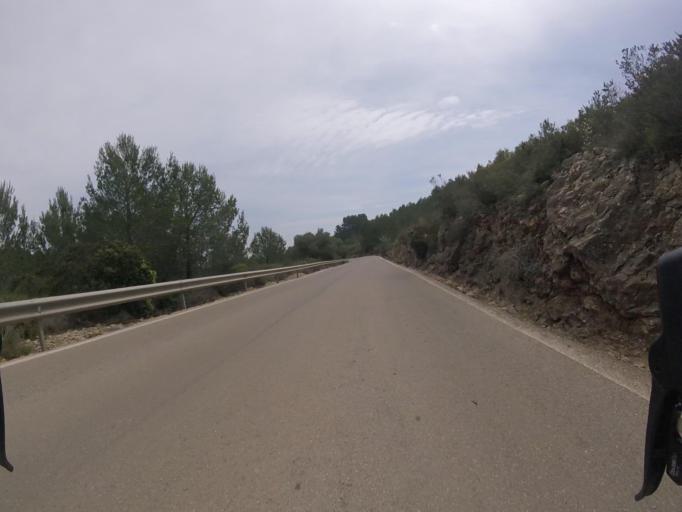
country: ES
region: Valencia
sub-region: Provincia de Castello
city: Cabanes
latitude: 40.1600
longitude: 0.0781
